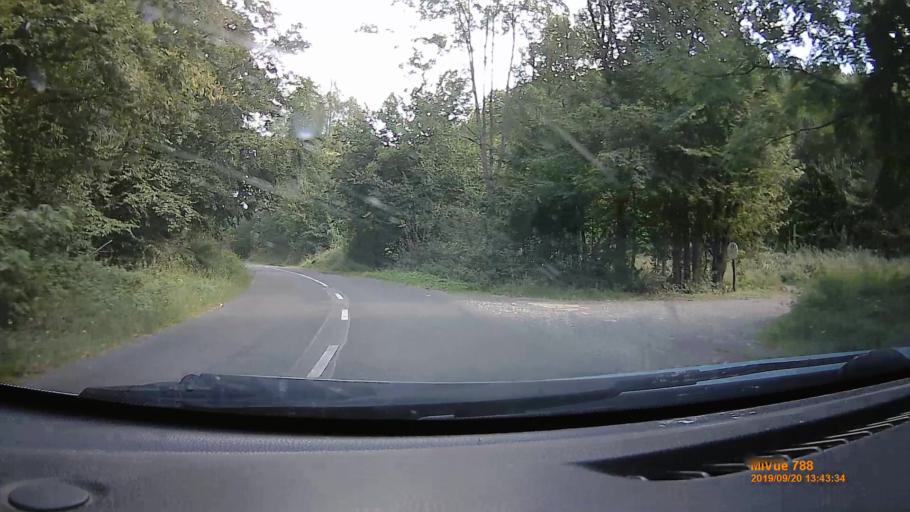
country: HU
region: Borsod-Abauj-Zemplen
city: Saly
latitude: 48.0577
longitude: 20.5555
